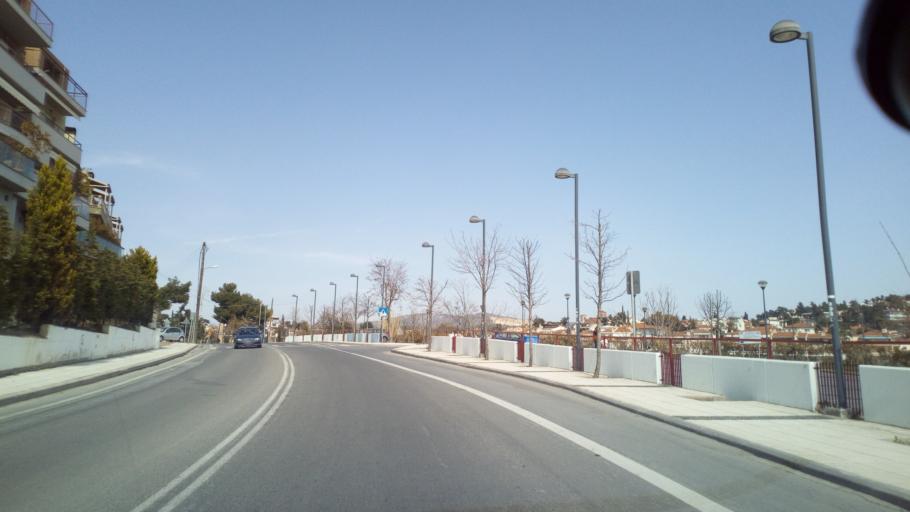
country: GR
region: Central Macedonia
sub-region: Nomos Thessalonikis
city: Panorama
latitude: 40.5853
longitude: 23.0355
